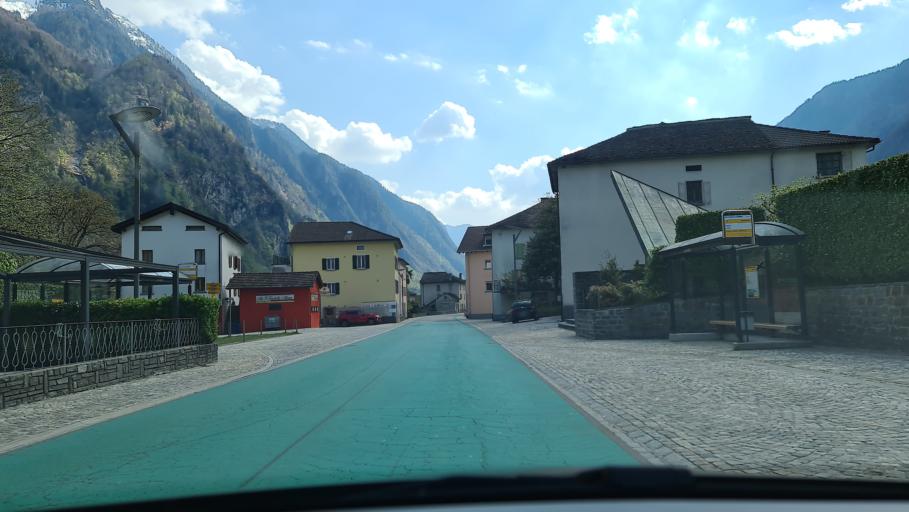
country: CH
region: Grisons
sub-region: Moesa District
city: Santa Maria in Calanca
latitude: 46.3135
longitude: 9.1962
